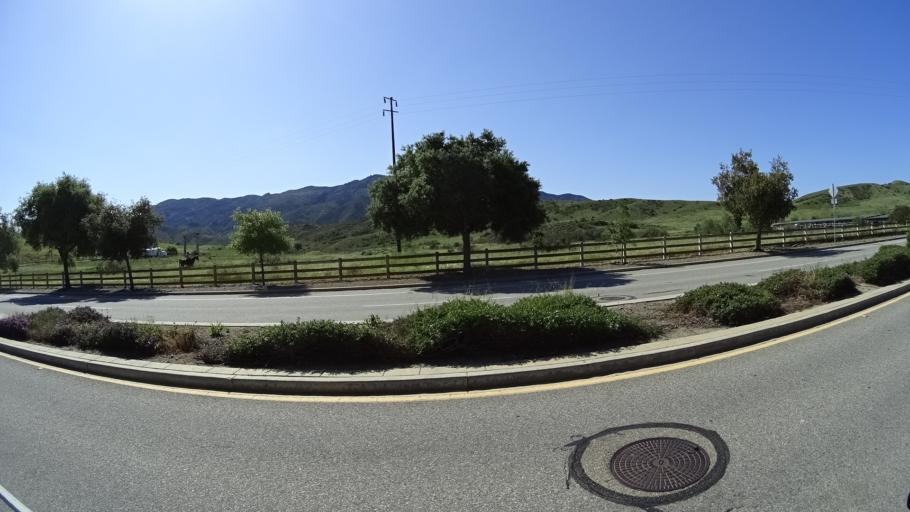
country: US
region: California
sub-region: Ventura County
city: Casa Conejo
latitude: 34.1568
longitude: -118.9744
